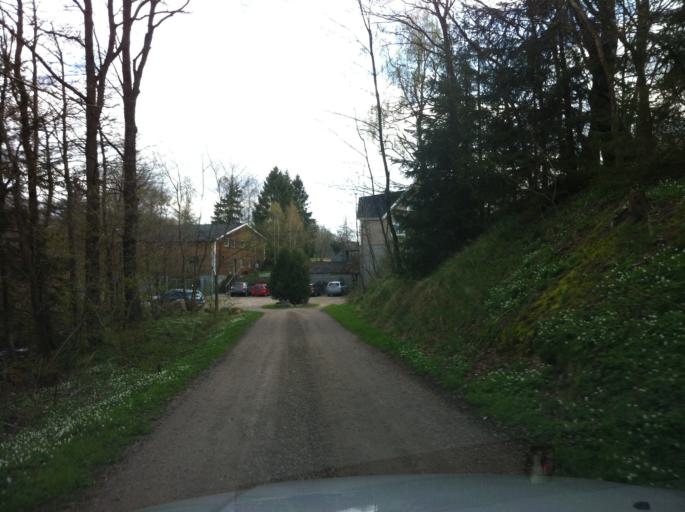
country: SE
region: Skane
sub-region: Hoors Kommun
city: Satofta
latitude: 55.9108
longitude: 13.6120
